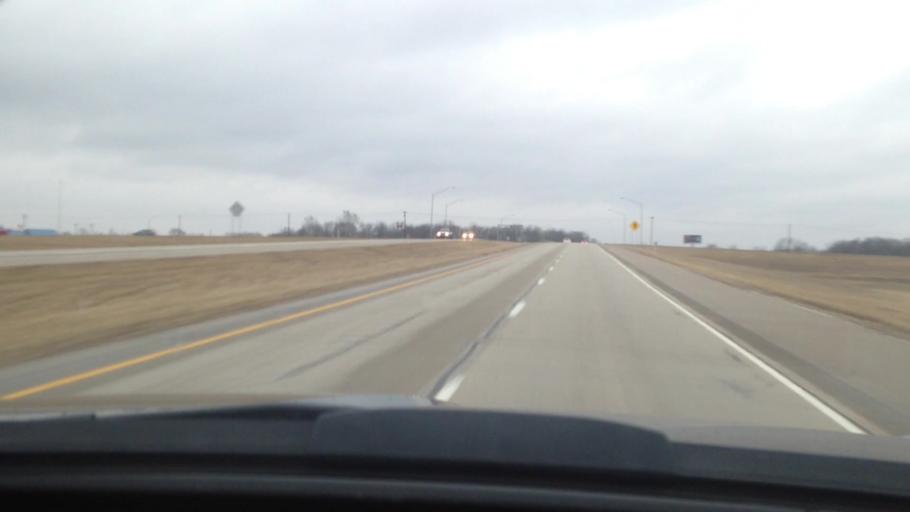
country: US
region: Indiana
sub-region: Delaware County
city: Muncie
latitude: 40.1816
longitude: -85.3366
